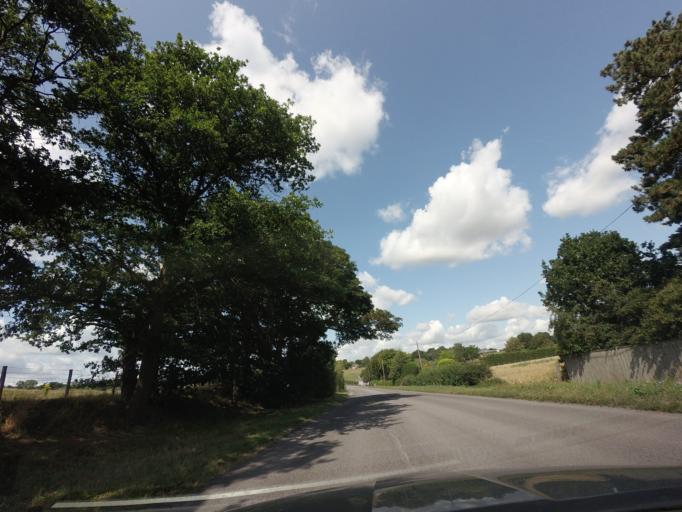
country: GB
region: England
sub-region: Kent
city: Harrietsham
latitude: 51.2633
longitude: 0.6073
